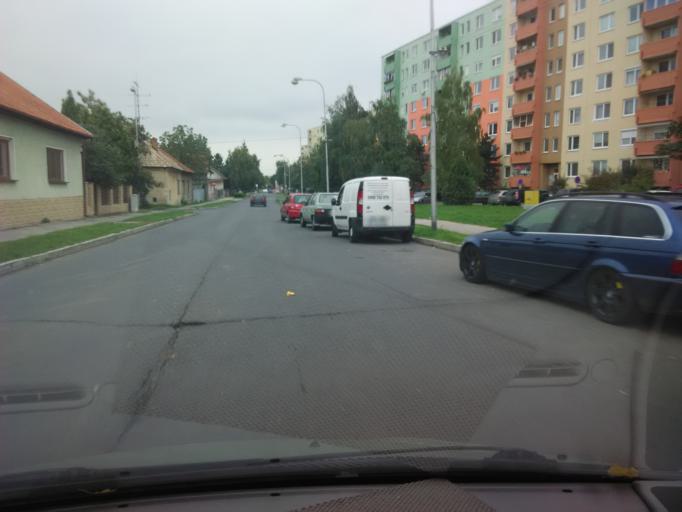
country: SK
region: Nitriansky
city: Levice
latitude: 48.2124
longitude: 18.6075
